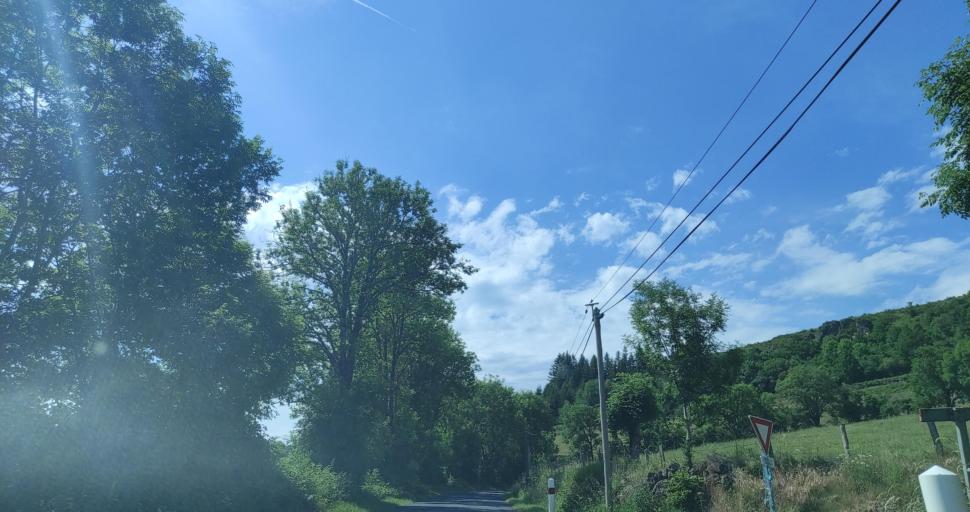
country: FR
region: Midi-Pyrenees
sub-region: Departement de l'Aveyron
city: Laguiole
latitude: 44.6596
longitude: 2.8580
